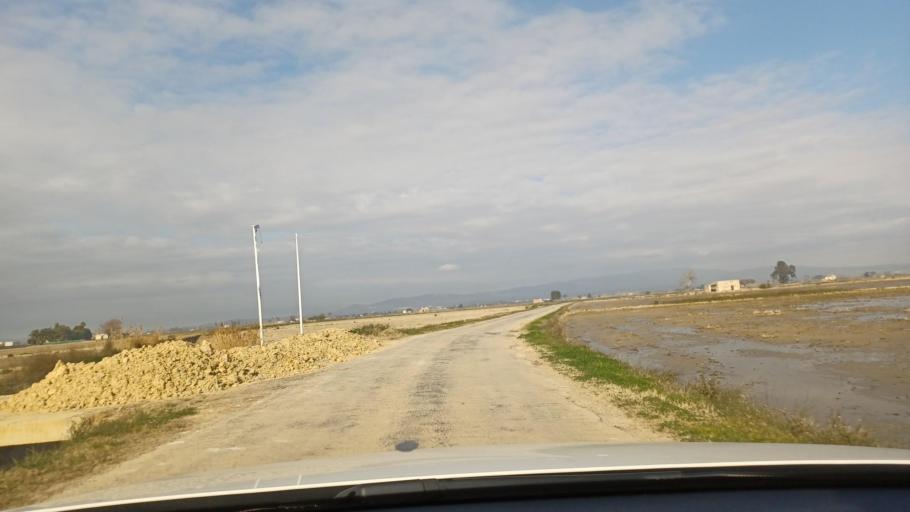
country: ES
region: Catalonia
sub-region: Provincia de Tarragona
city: Deltebre
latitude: 40.6880
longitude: 0.6523
